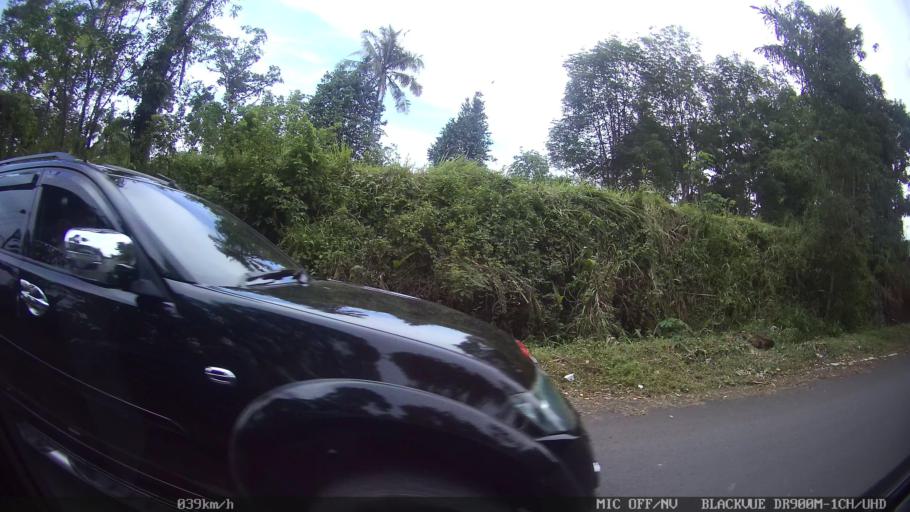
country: ID
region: Lampung
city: Bandarlampung
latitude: -5.4294
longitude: 105.2013
